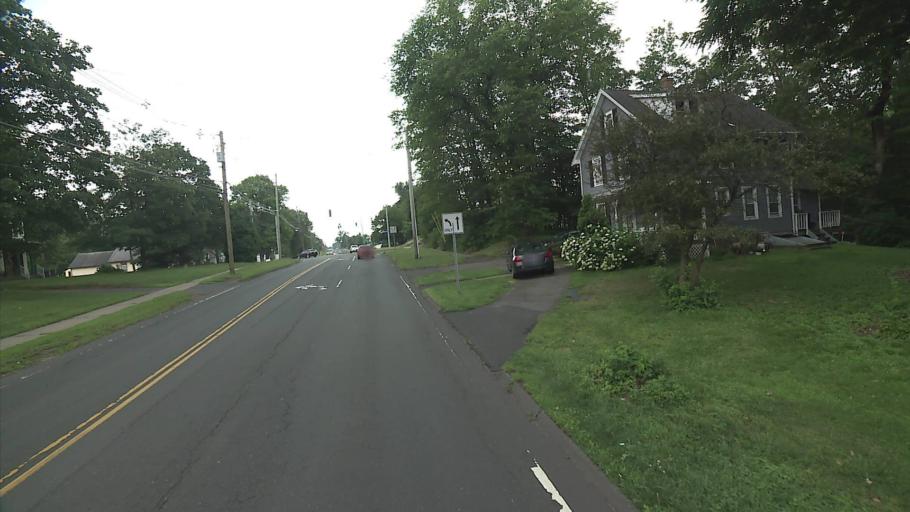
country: US
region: Connecticut
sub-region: Hartford County
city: Newington
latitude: 41.7121
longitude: -72.7368
